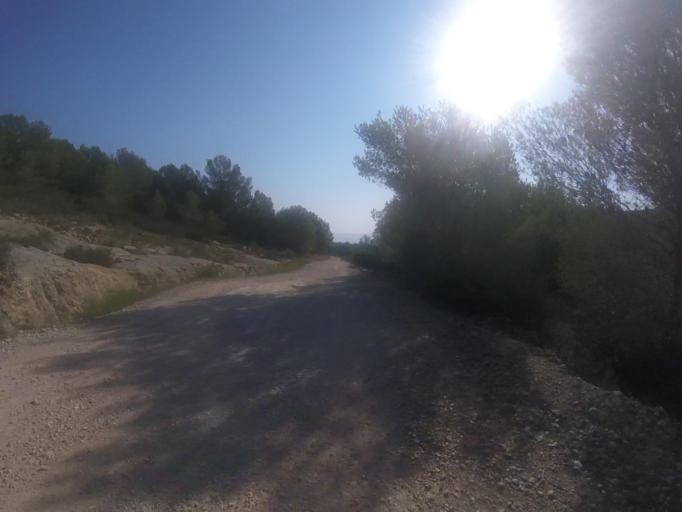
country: ES
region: Valencia
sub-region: Provincia de Castello
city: Peniscola
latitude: 40.3313
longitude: 0.3624
